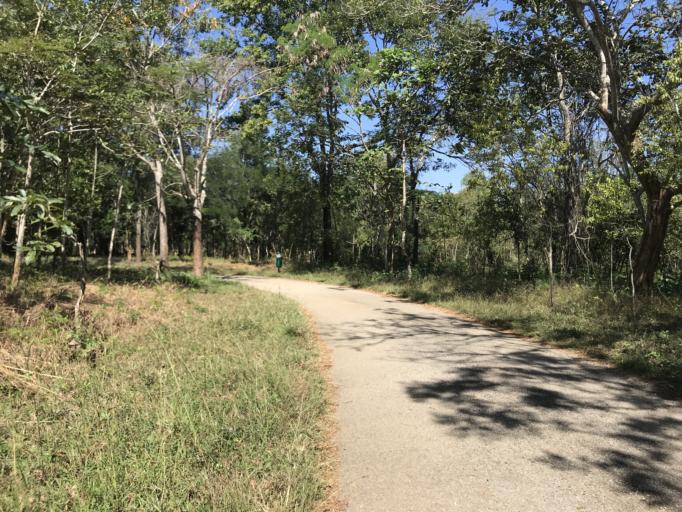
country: IN
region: Karnataka
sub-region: Mysore
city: Sargur
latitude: 11.9407
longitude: 76.2699
